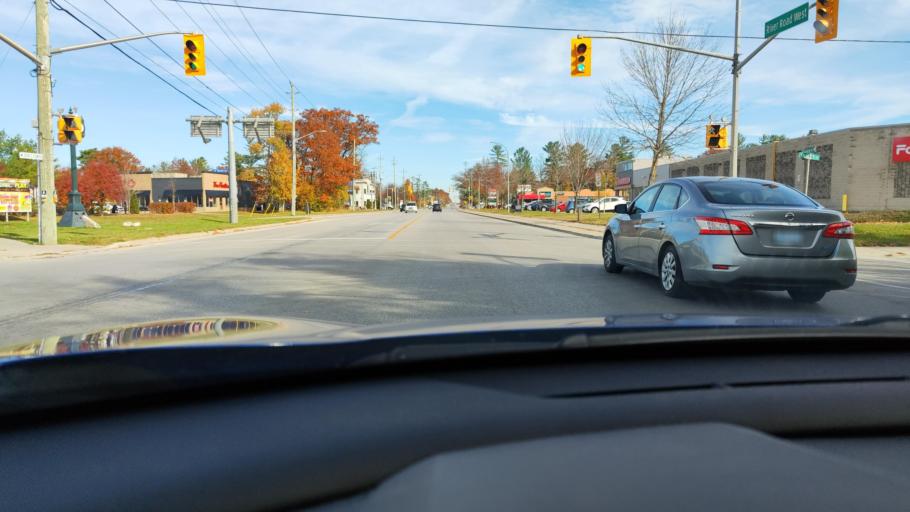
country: CA
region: Ontario
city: Wasaga Beach
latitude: 44.5232
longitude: -80.0042
